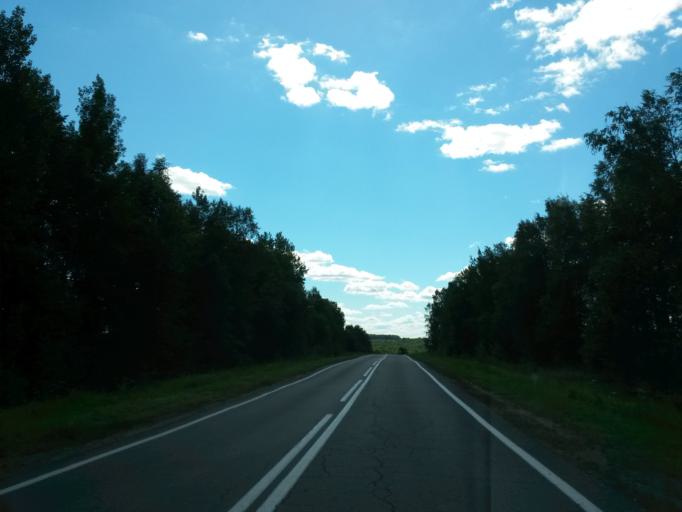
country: RU
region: Jaroslavl
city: Tutayev
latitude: 57.9459
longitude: 39.4969
